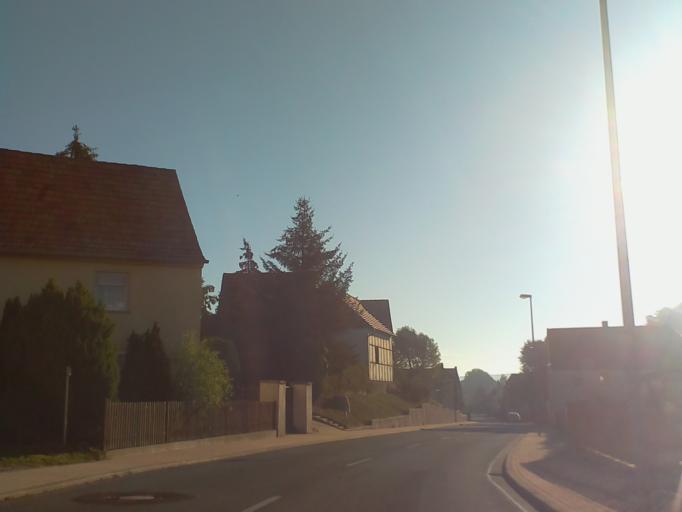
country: DE
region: Thuringia
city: Saara
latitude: 50.8534
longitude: 11.9519
